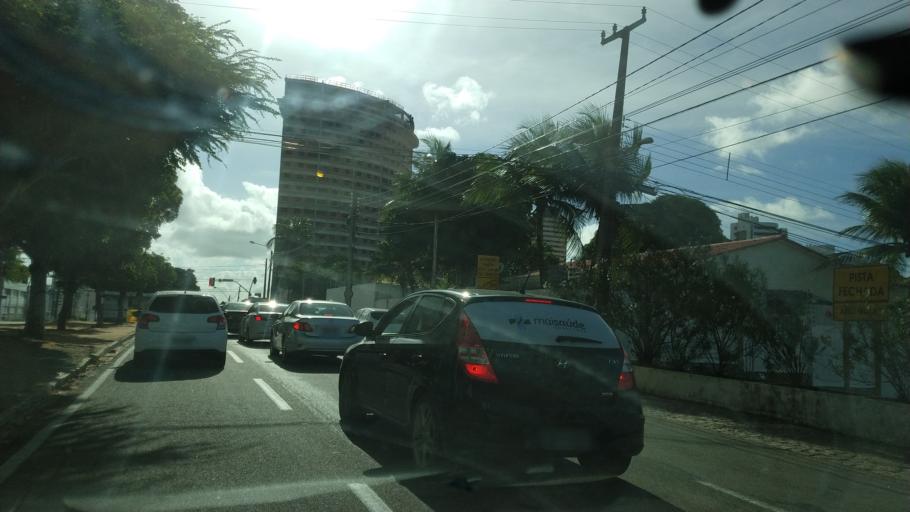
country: BR
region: Rio Grande do Norte
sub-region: Natal
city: Natal
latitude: -5.8077
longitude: -35.2023
